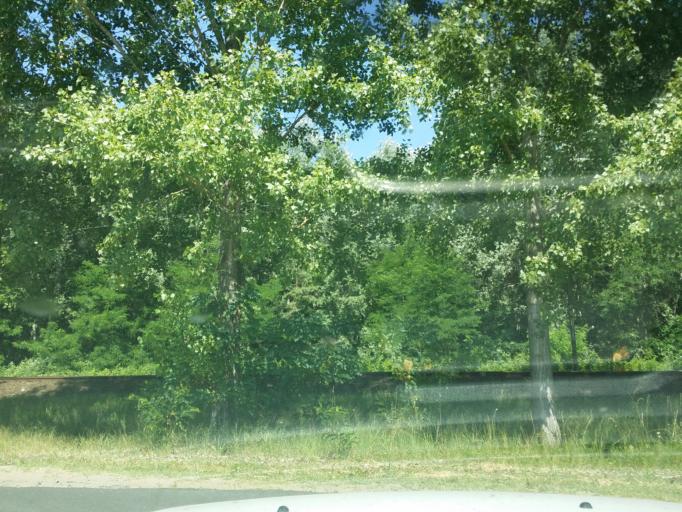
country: HU
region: Bacs-Kiskun
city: Jaszszentlaszlo
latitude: 46.5748
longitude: 19.7697
